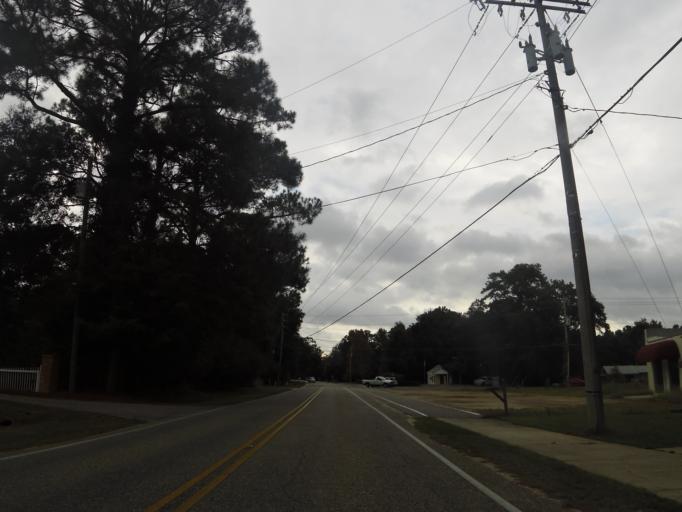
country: US
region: Alabama
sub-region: Baldwin County
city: Point Clear
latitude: 30.4715
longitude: -87.9177
